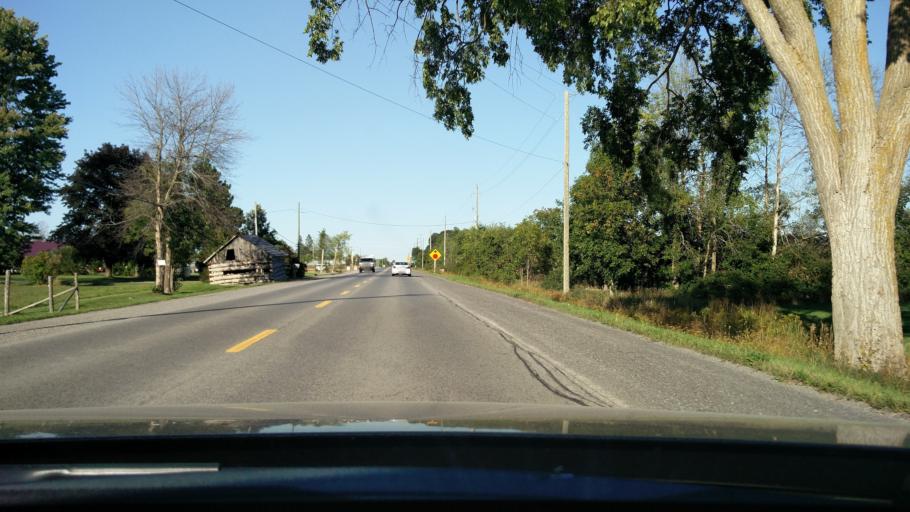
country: CA
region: Ontario
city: Carleton Place
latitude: 45.1249
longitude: -75.9494
